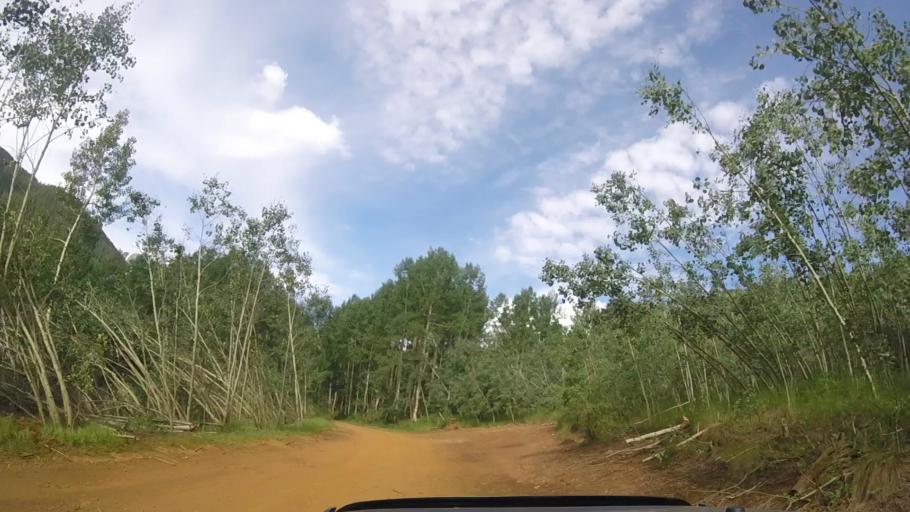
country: US
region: Colorado
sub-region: San Miguel County
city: Telluride
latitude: 37.8588
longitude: -107.8103
